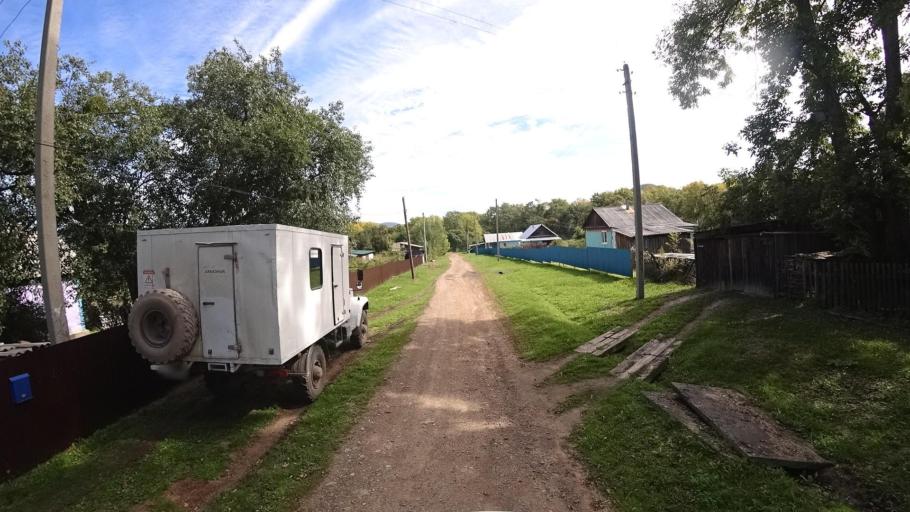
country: RU
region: Primorskiy
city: Yakovlevka
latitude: 44.3960
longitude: 133.6007
